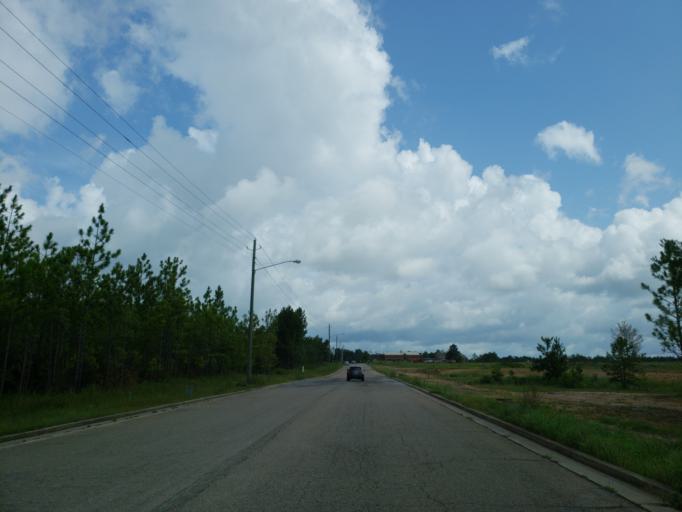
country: US
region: Mississippi
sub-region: Lamar County
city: West Hattiesburg
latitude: 31.3143
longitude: -89.3938
